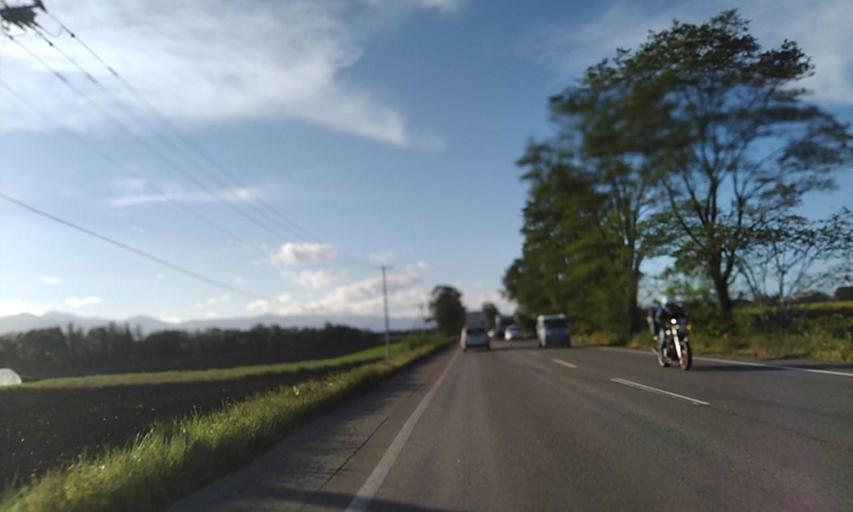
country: JP
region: Hokkaido
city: Obihiro
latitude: 42.9238
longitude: 142.9904
